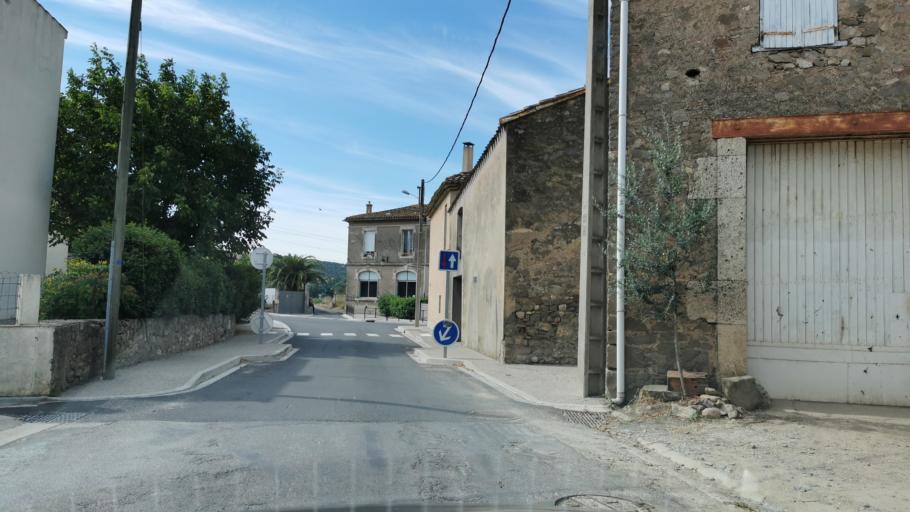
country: FR
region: Languedoc-Roussillon
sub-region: Departement de l'Herault
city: Olonzac
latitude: 43.2668
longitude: 2.7226
